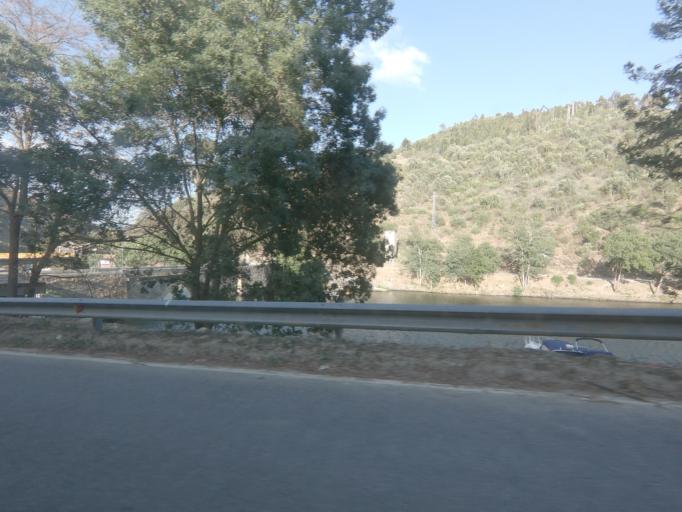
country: PT
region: Viseu
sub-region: Tabuaco
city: Tabuaco
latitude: 41.1567
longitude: -7.5829
